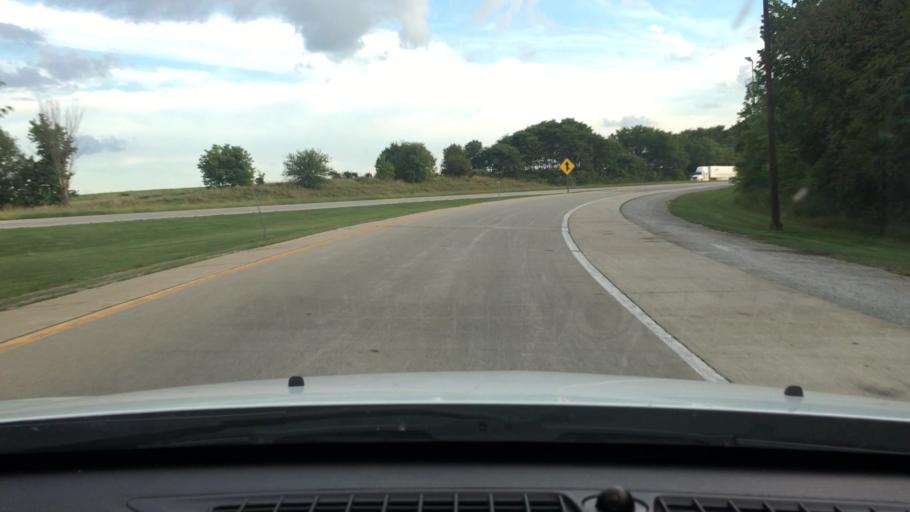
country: US
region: Illinois
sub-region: McLean County
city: Twin Grove
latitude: 40.3569
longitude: -89.1106
